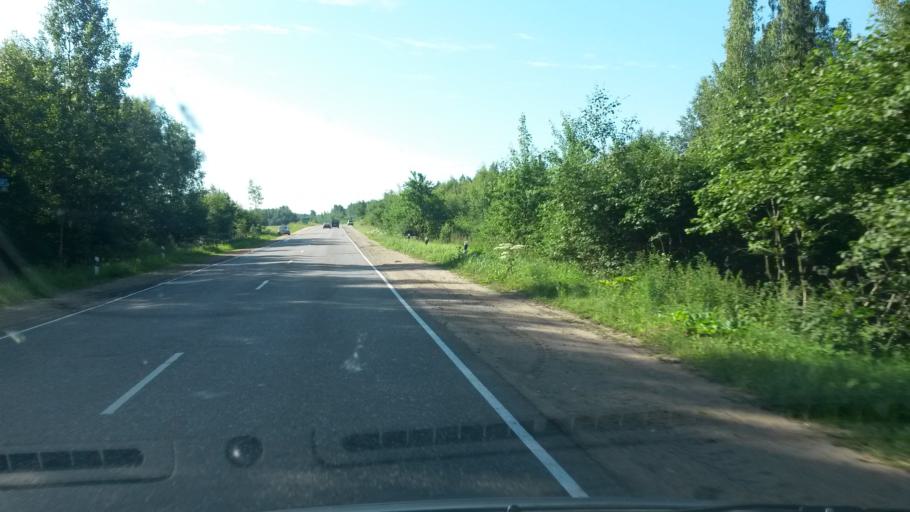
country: RU
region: Ivanovo
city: Novo-Talitsy
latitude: 57.0437
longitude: 40.7409
